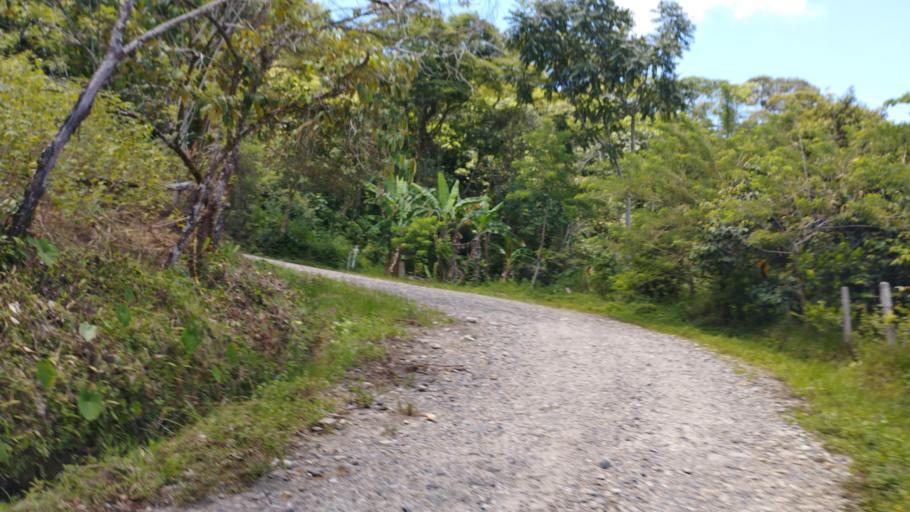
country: CO
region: Boyaca
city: San Luis de Gaceno
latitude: 4.7850
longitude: -73.1205
